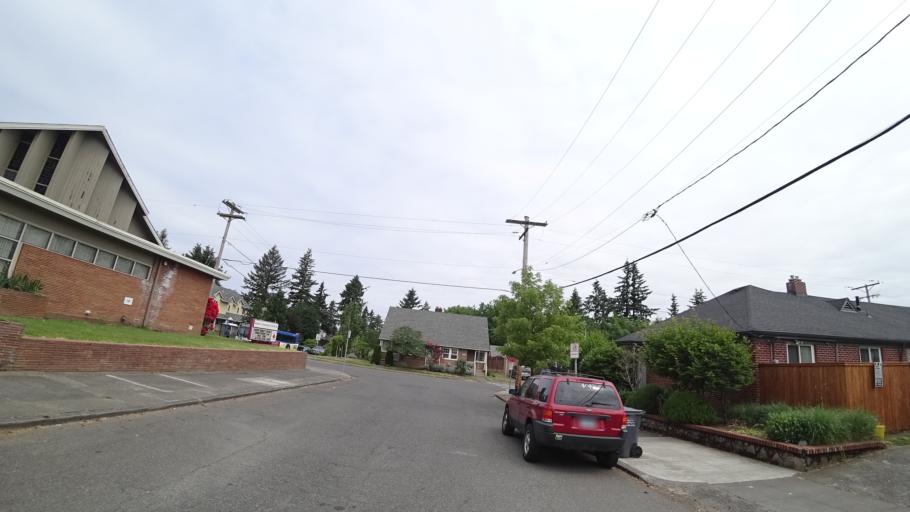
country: US
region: Oregon
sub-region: Multnomah County
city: Portland
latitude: 45.5624
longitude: -122.6379
